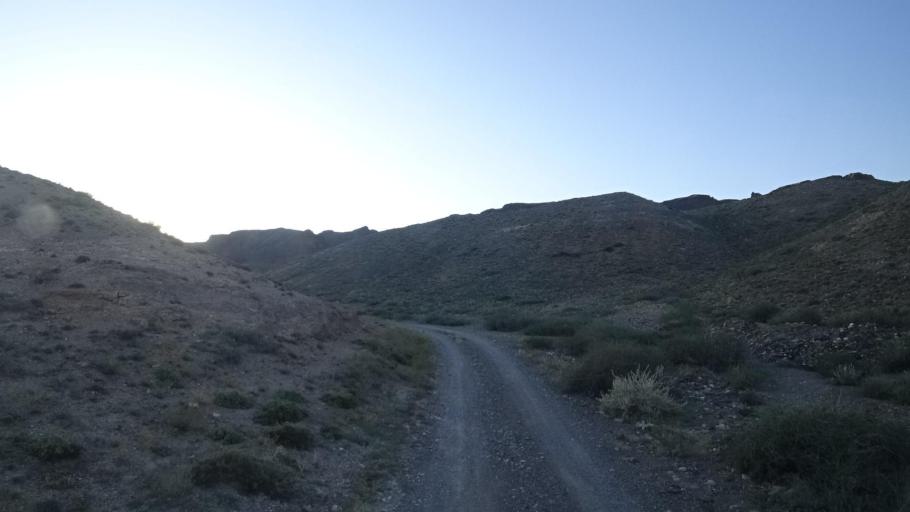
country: KZ
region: Almaty Oblysy
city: Kegen
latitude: 43.2725
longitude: 78.9746
